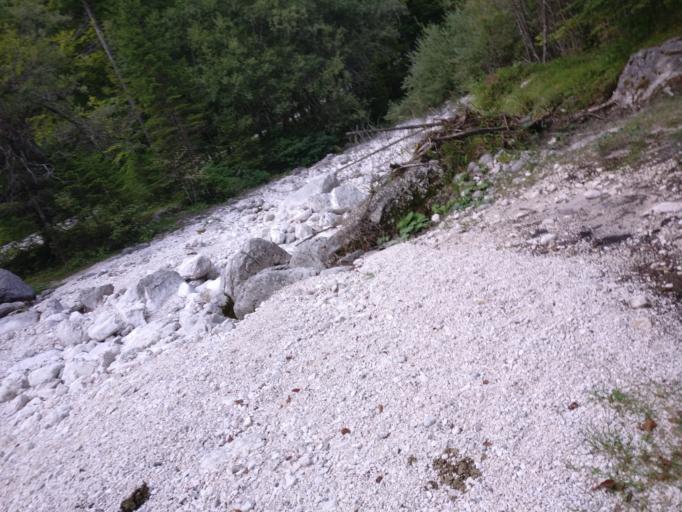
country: SI
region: Kranjska Gora
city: Mojstrana
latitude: 46.4178
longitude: 13.8584
